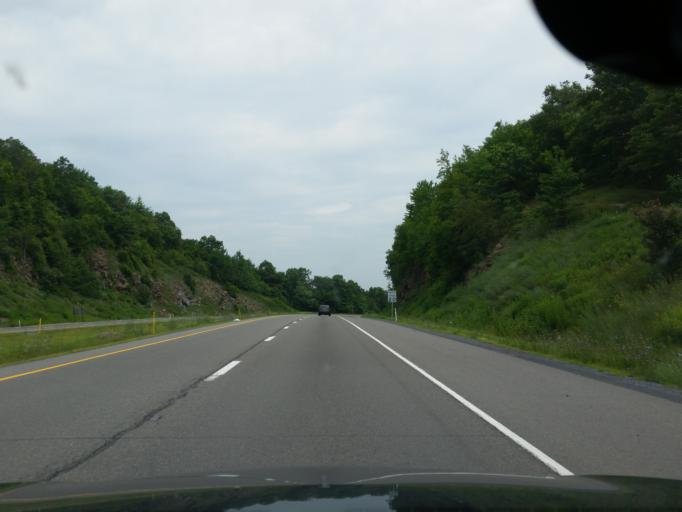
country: US
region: Pennsylvania
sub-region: Mifflin County
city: Milroy
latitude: 40.7663
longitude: -77.6161
